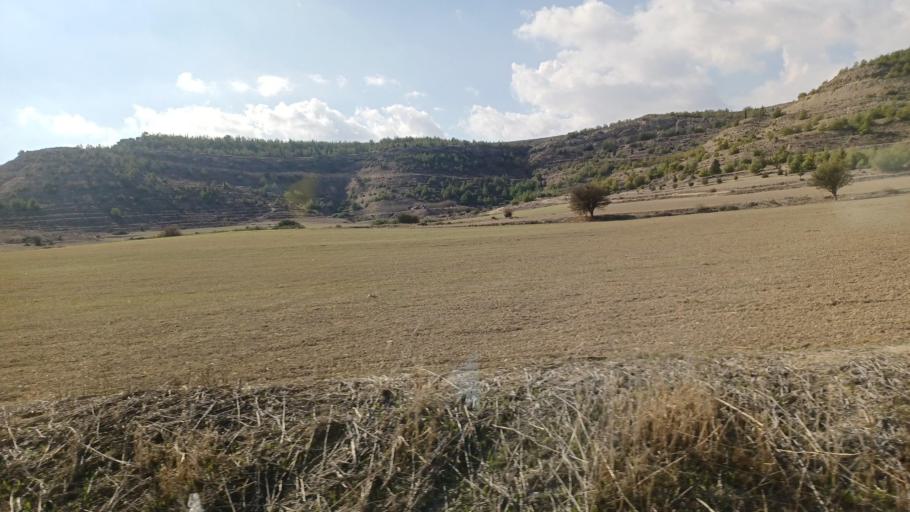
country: CY
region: Larnaka
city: Voroklini
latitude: 34.9970
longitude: 33.6541
